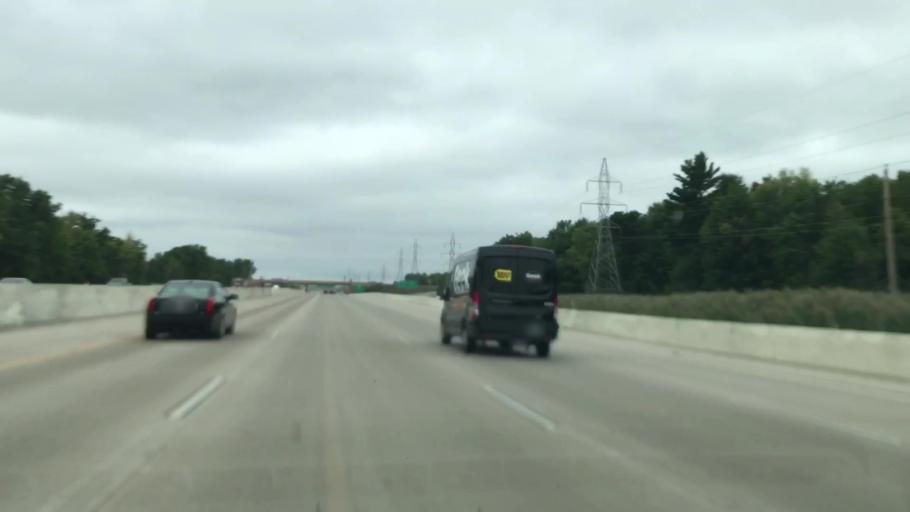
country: US
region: Wisconsin
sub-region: Brown County
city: Suamico
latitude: 44.5819
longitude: -88.0487
